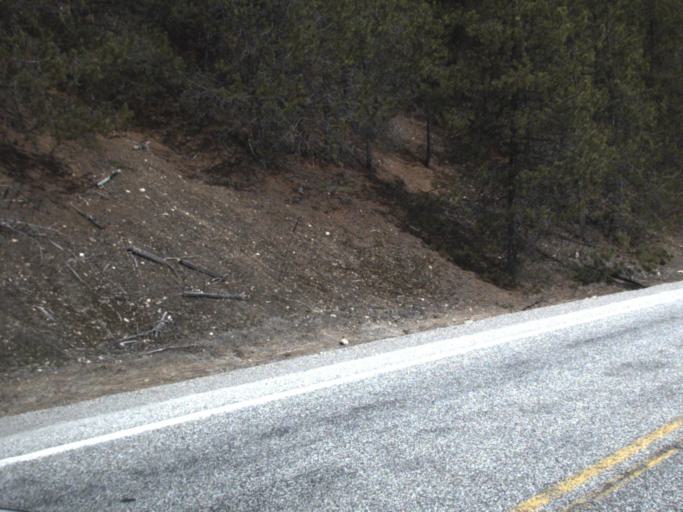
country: US
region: Washington
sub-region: Stevens County
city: Chewelah
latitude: 48.5476
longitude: -117.5743
